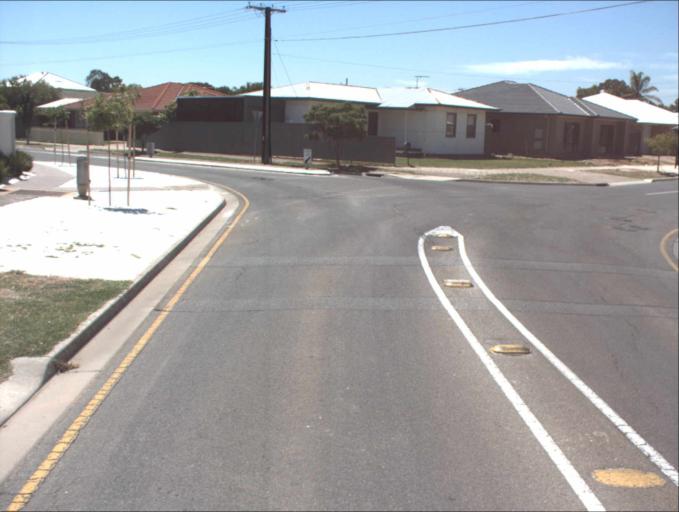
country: AU
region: South Australia
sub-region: Port Adelaide Enfield
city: Klemzig
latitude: -34.8698
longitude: 138.6276
